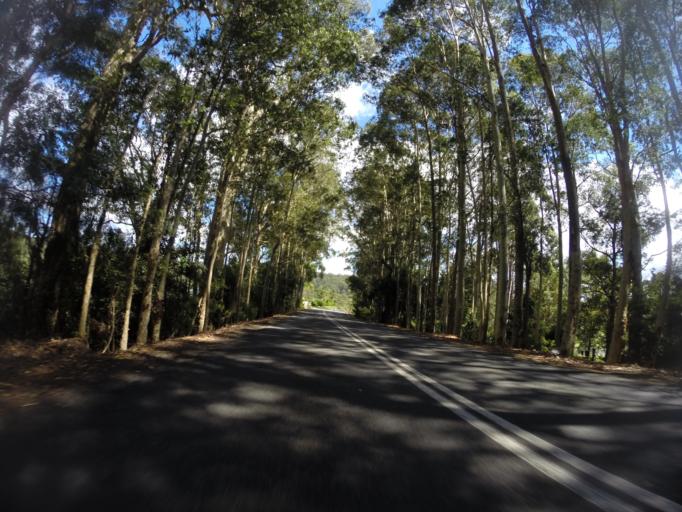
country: AU
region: New South Wales
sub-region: Eurobodalla
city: Batemans Bay
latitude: -35.6514
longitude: 150.2455
